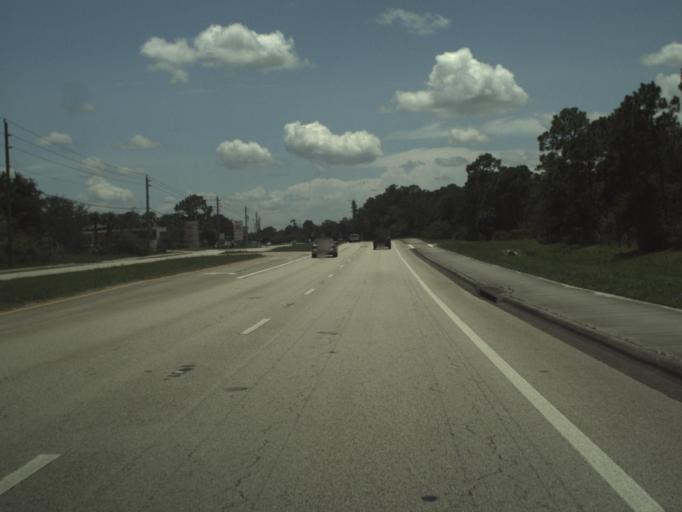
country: US
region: Florida
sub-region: Martin County
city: Palm City
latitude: 27.1359
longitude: -80.2498
